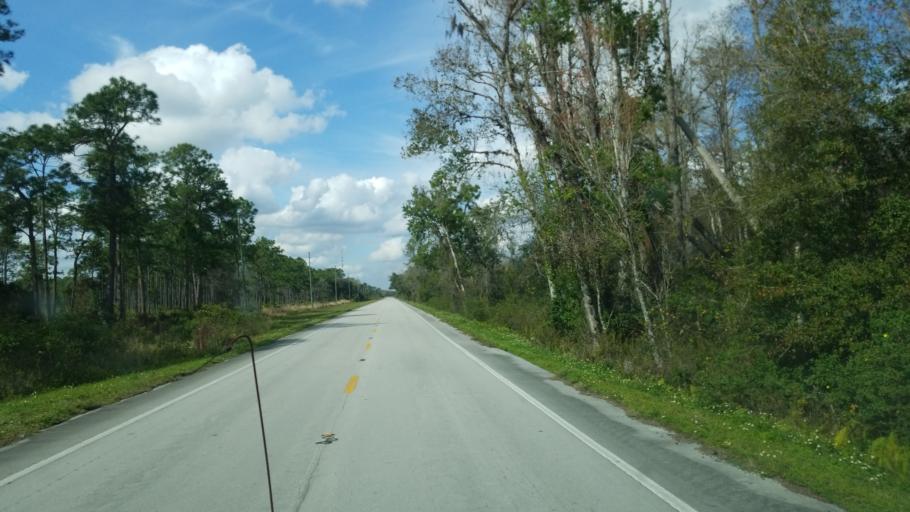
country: US
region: Florida
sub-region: Brevard County
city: June Park
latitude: 27.9884
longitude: -81.0153
